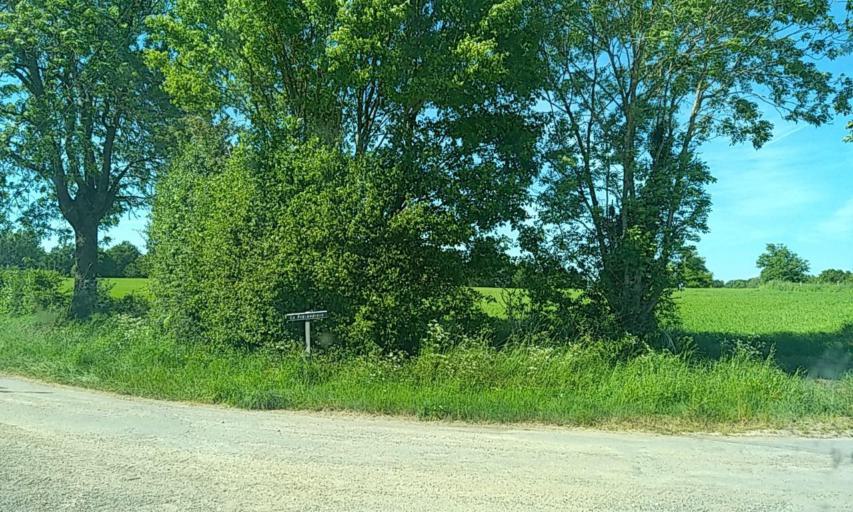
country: FR
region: Poitou-Charentes
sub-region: Departement des Deux-Sevres
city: Boisme
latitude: 46.7907
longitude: -0.4630
